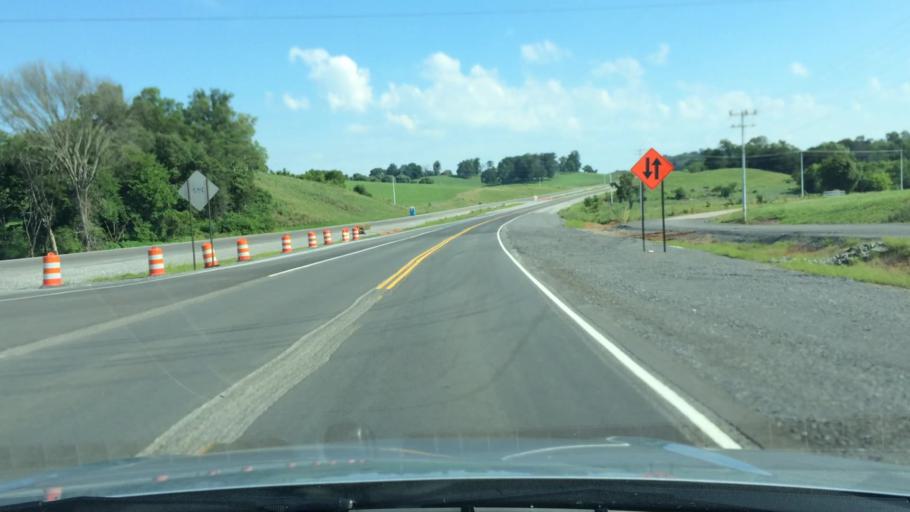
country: US
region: Tennessee
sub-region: Jefferson County
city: White Pine
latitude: 36.1423
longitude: -83.3437
